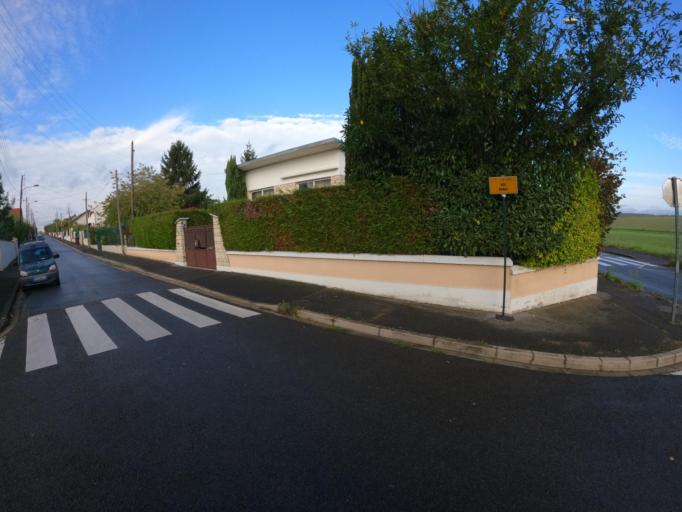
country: FR
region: Ile-de-France
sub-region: Departement de Seine-et-Marne
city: Brou-sur-Chantereine
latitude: 48.8945
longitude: 2.6248
